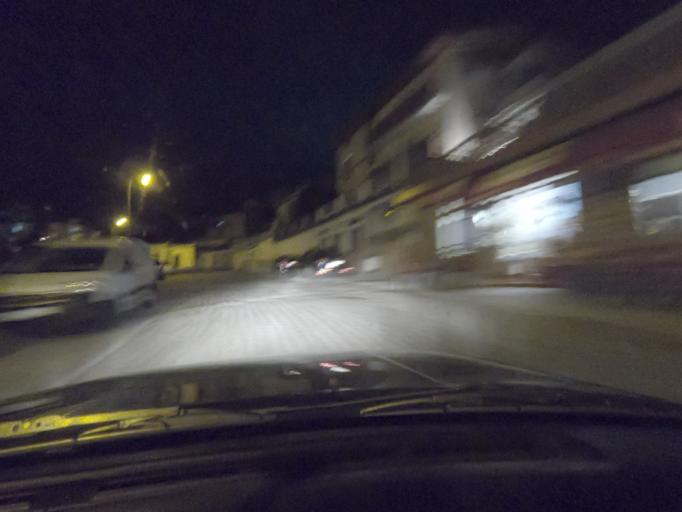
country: PT
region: Vila Real
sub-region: Peso da Regua
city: Peso da Regua
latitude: 41.1650
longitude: -7.7816
